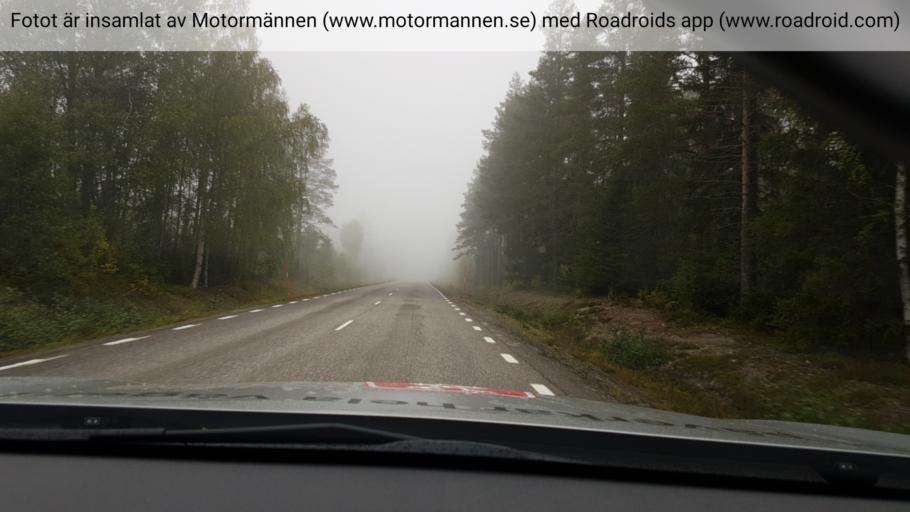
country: SE
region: Vaesterbotten
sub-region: Umea Kommun
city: Ersmark
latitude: 64.1161
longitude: 20.1666
